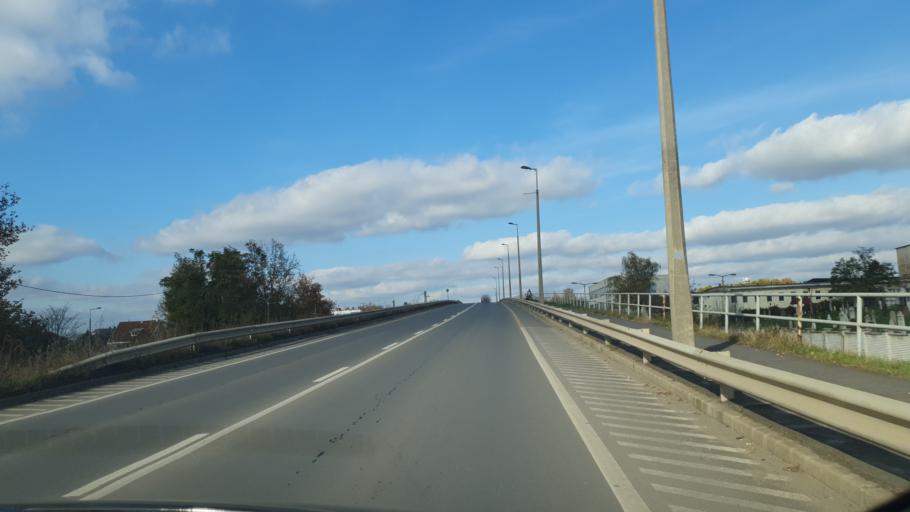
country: HU
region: Szabolcs-Szatmar-Bereg
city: Kisvarda
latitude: 48.2117
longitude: 22.0859
